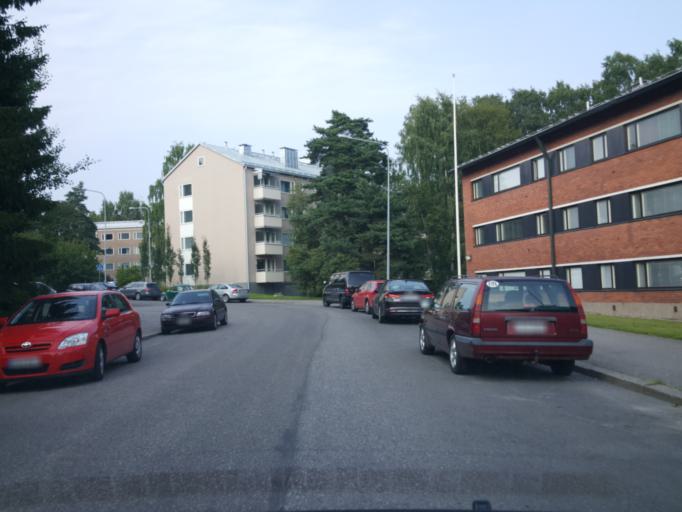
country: FI
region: Uusimaa
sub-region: Helsinki
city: Teekkarikylae
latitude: 60.2184
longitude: 24.8582
